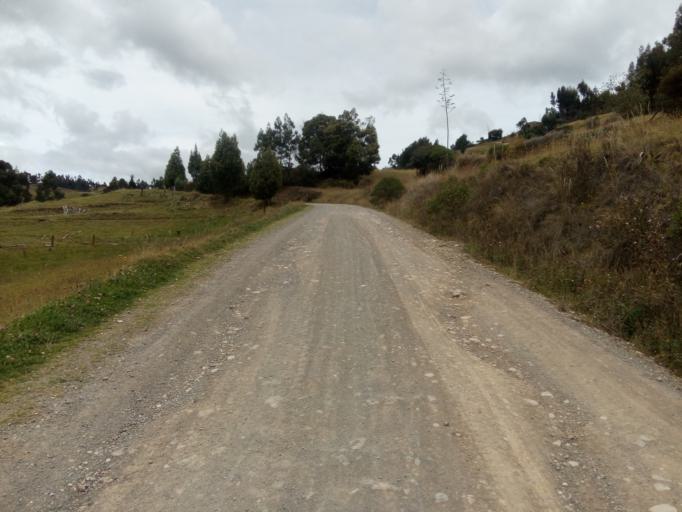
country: CO
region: Boyaca
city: Gameza
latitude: 5.8183
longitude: -72.8023
